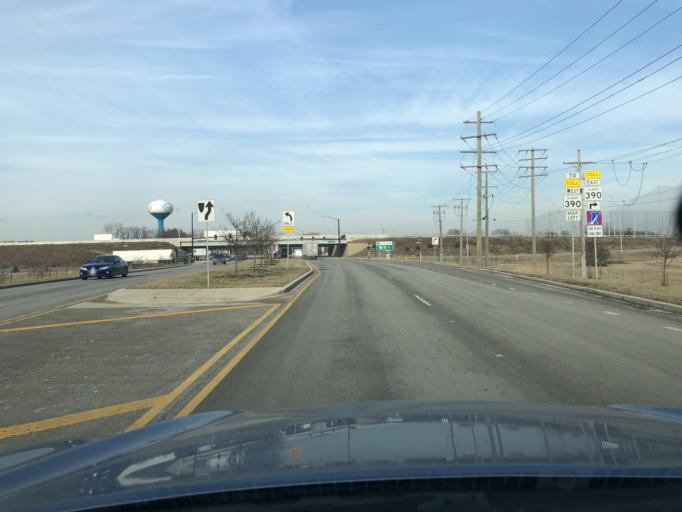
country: US
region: Illinois
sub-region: DuPage County
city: Itasca
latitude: 41.9810
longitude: -87.9981
